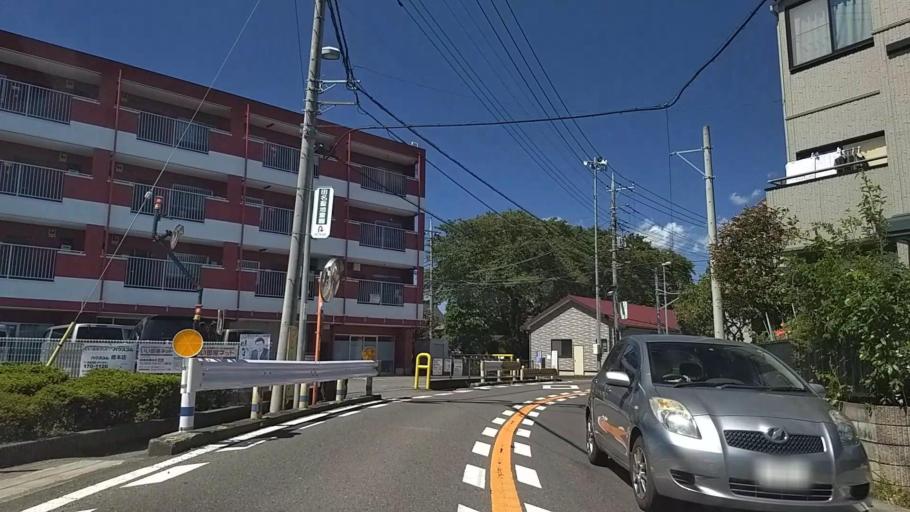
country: JP
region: Kanagawa
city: Zama
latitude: 35.5419
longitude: 139.3385
